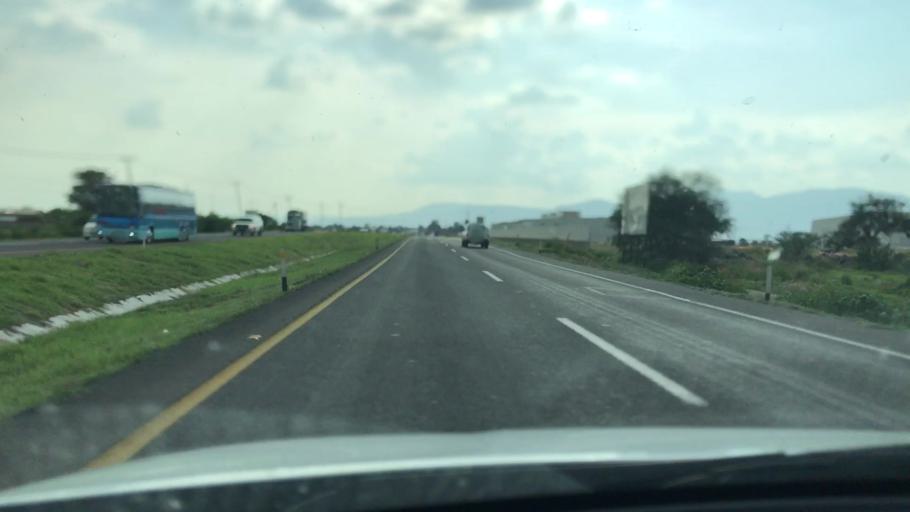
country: MX
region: Guanajuato
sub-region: Penjamo
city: Estacion Corralejo
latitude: 20.4517
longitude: -101.5781
